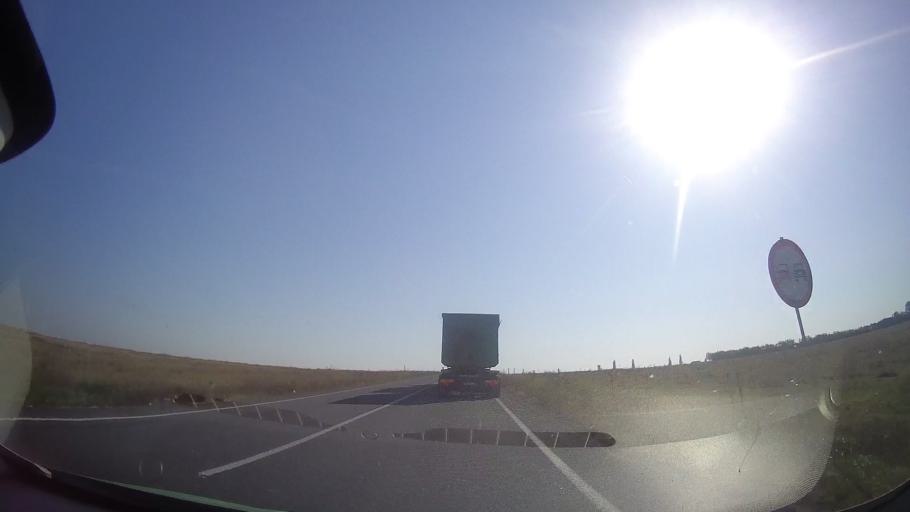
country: RO
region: Timis
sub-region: Comuna Ghizela
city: Ghizela
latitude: 45.7767
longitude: 21.6910
